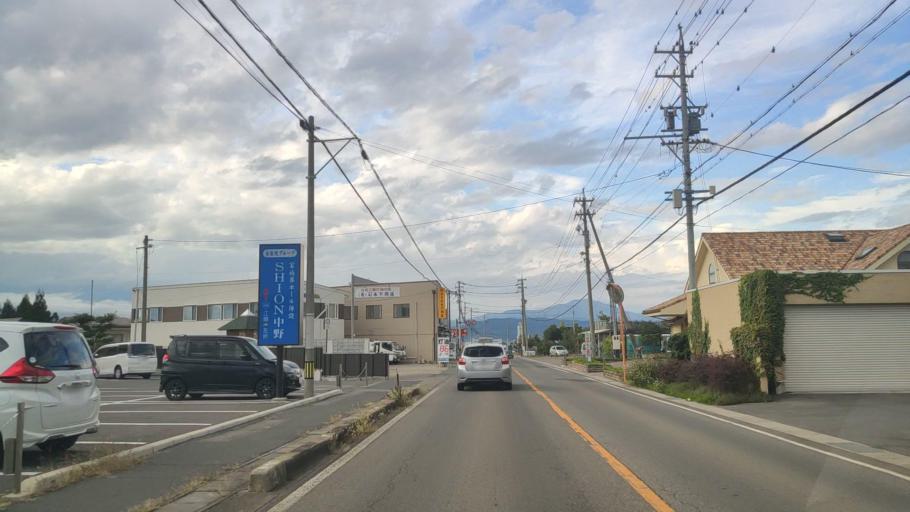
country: JP
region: Nagano
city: Suzaka
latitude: 36.6801
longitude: 138.3173
